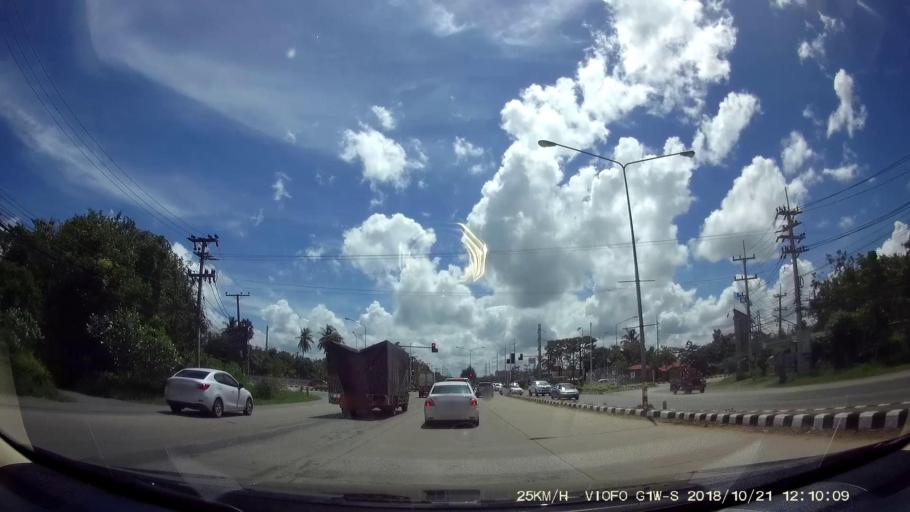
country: TH
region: Chaiyaphum
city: Chatturat
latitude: 15.4148
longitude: 101.8335
